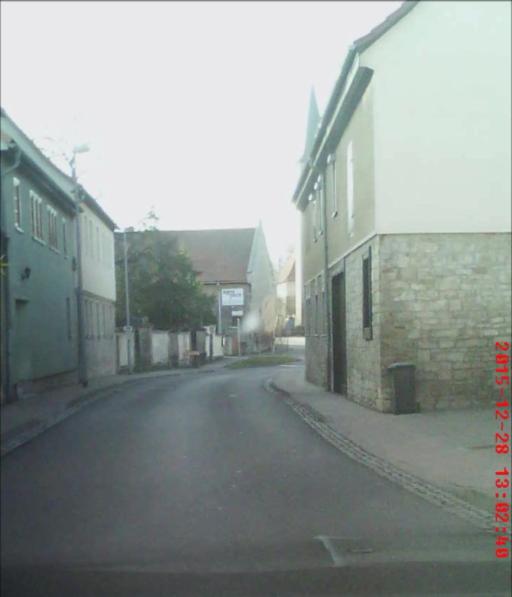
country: DE
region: Thuringia
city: Niederrossla
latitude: 51.0374
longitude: 11.4880
